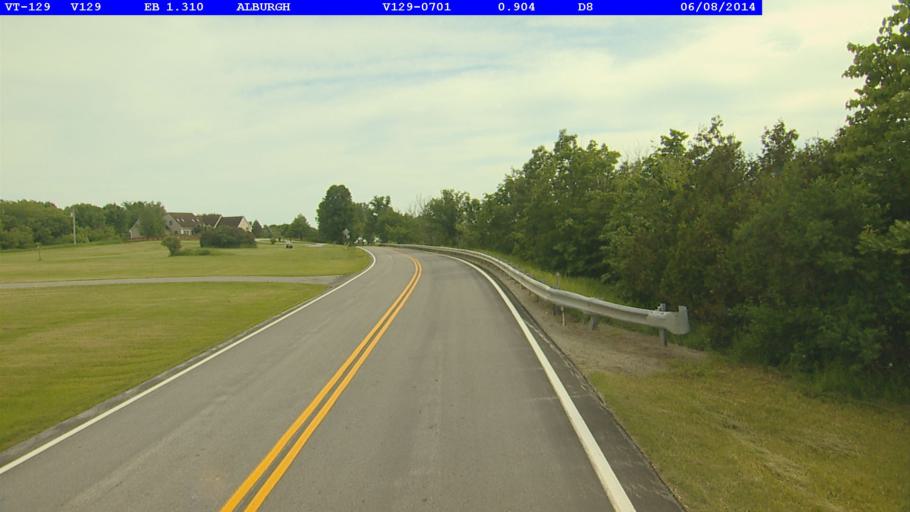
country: US
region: Vermont
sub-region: Grand Isle County
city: North Hero
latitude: 44.8983
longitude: -73.3038
